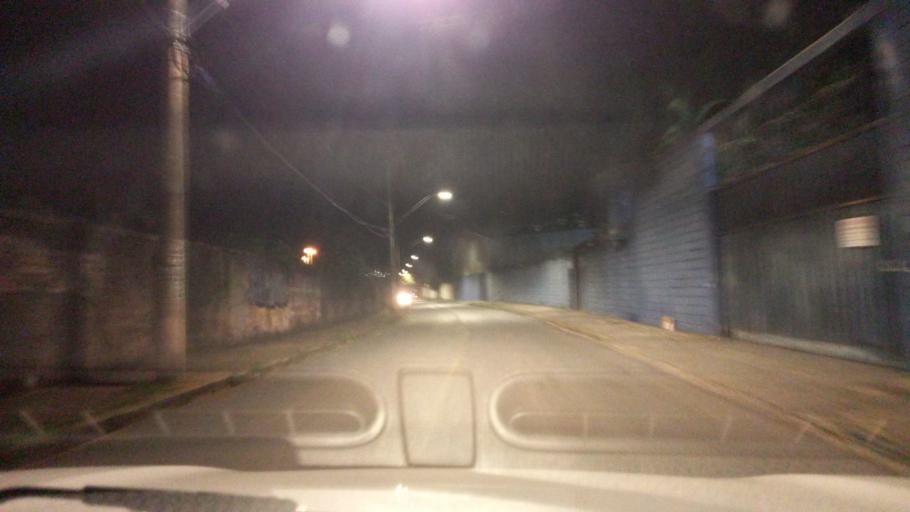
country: BR
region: Minas Gerais
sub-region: Belo Horizonte
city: Belo Horizonte
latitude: -19.8591
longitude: -43.9224
